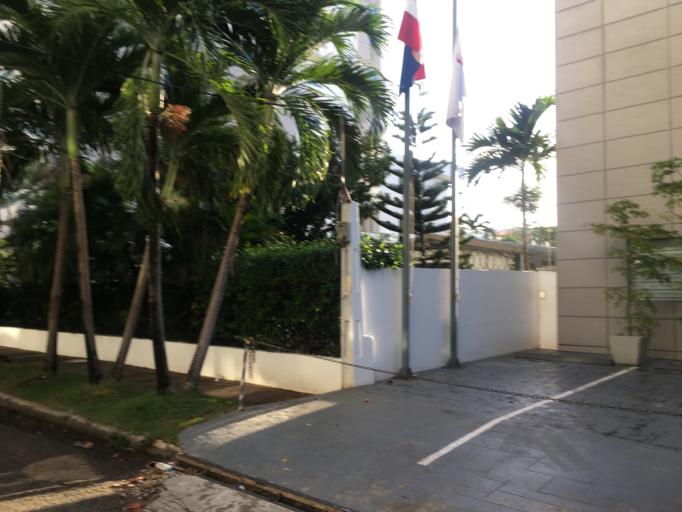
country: DO
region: Nacional
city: La Julia
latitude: 18.4617
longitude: -69.9328
